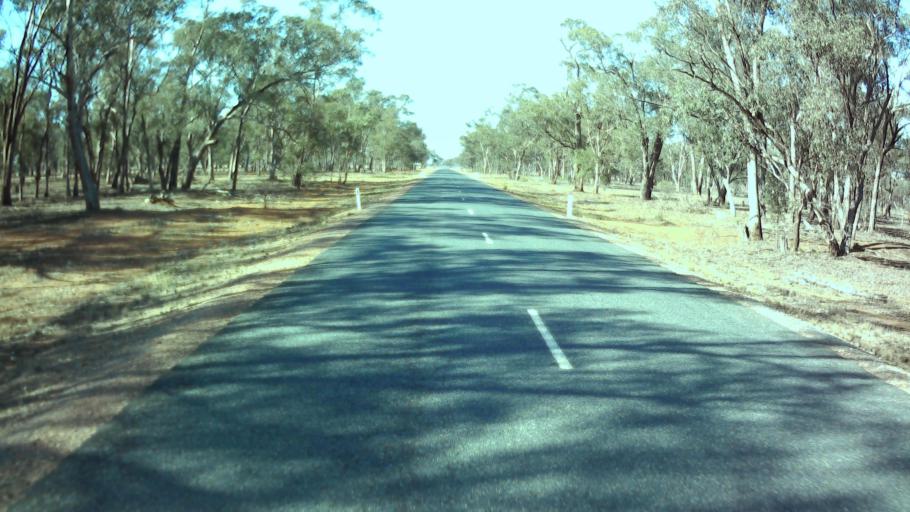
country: AU
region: New South Wales
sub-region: Weddin
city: Grenfell
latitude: -34.0637
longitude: 147.9082
